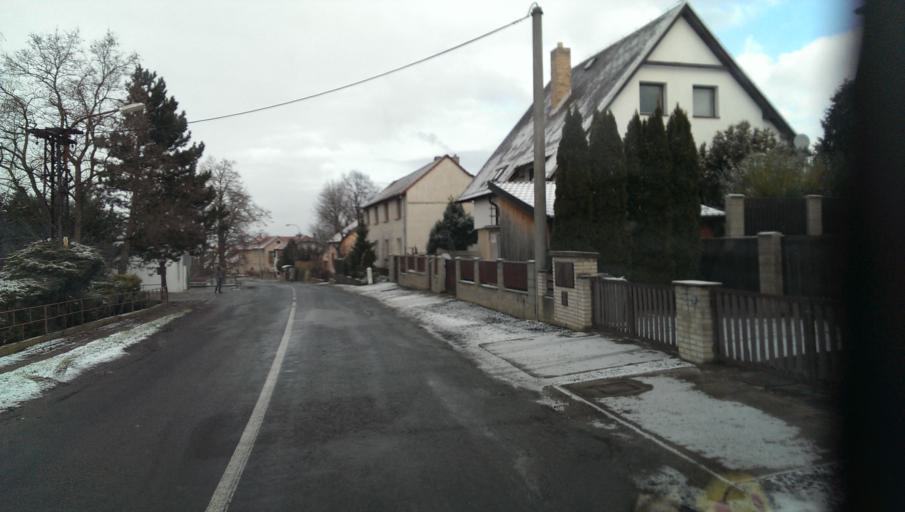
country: CZ
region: Ustecky
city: Trebenice
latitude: 50.4335
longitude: 14.0046
